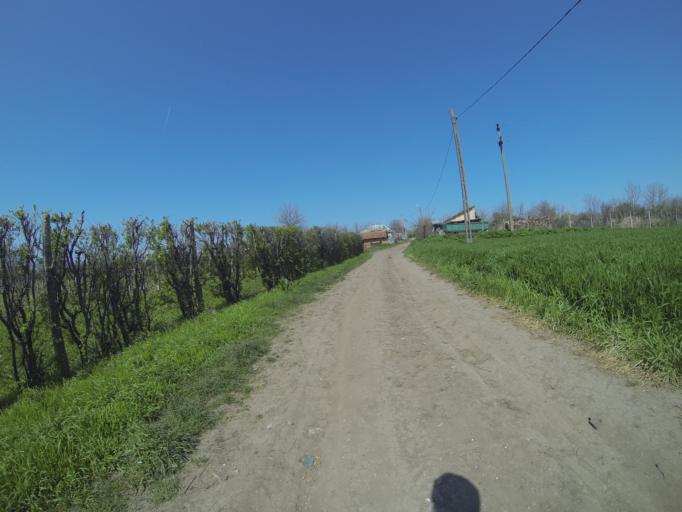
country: RO
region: Dolj
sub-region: Comuna Segarcea
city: Segarcea
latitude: 44.0979
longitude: 23.7303
